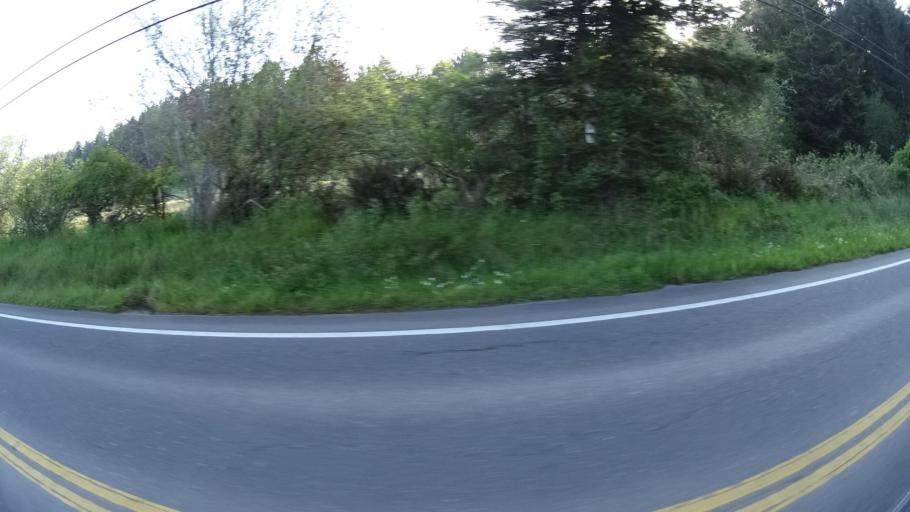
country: US
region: California
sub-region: Humboldt County
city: Myrtletown
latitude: 40.7787
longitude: -124.0751
